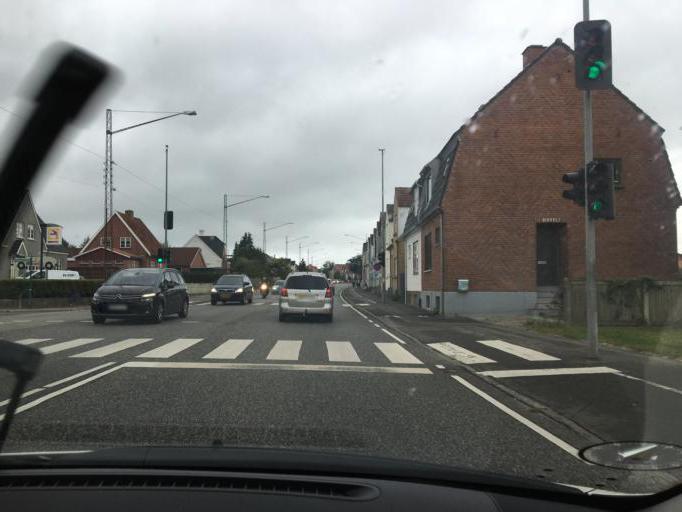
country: DK
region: South Denmark
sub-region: Middelfart Kommune
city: Middelfart
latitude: 55.4986
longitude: 9.7436
